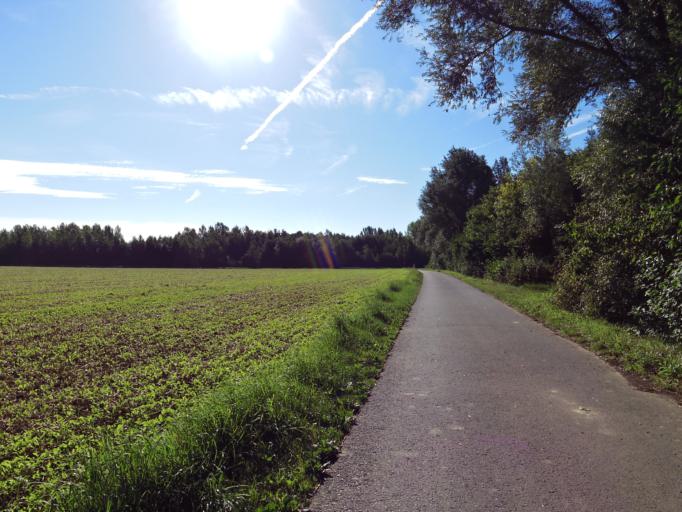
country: DE
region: North Rhine-Westphalia
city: Niedermerz
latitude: 50.8528
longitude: 6.2571
